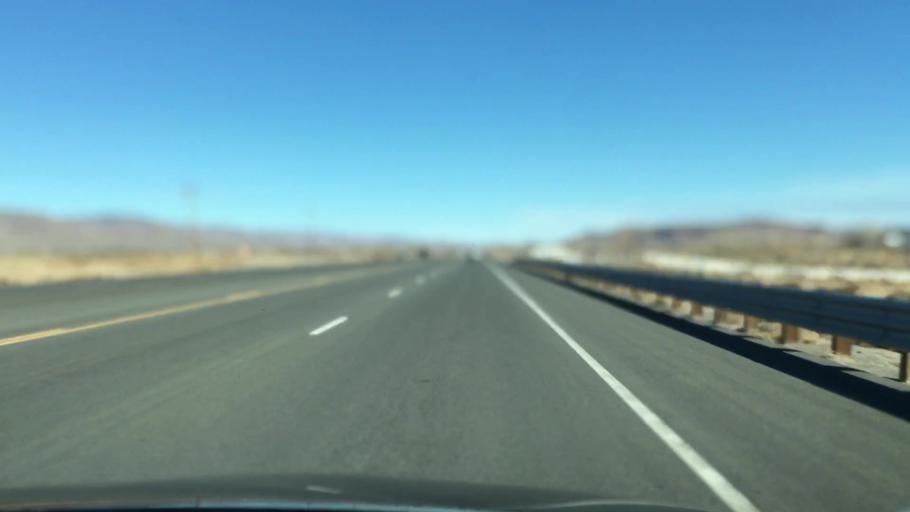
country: US
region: Nevada
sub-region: Lyon County
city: Dayton
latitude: 39.2820
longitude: -119.5511
